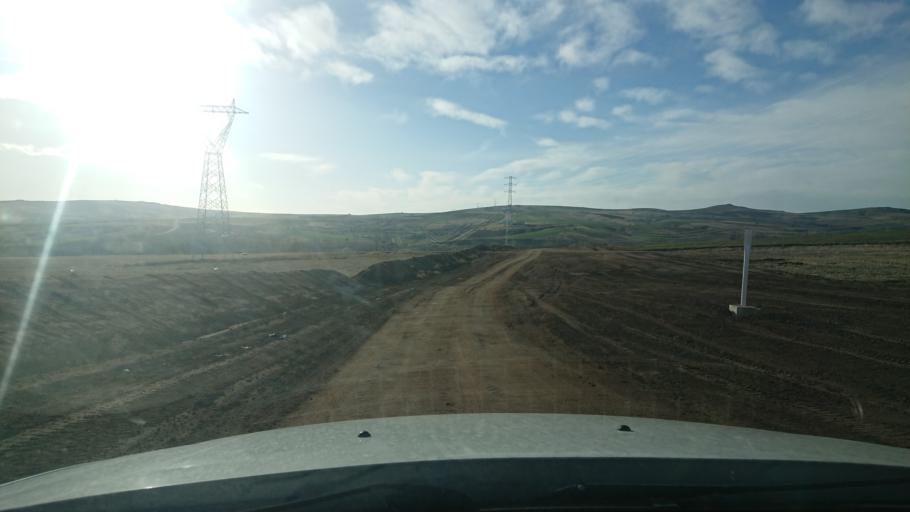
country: TR
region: Aksaray
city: Agacoren
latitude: 38.8669
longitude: 33.9398
